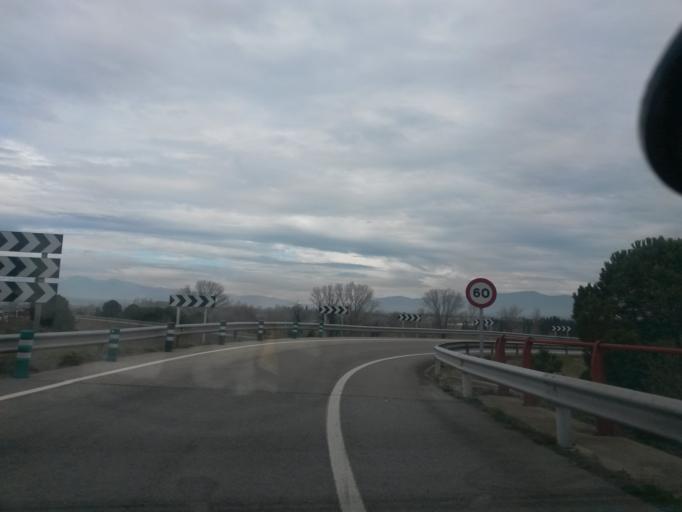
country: ES
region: Catalonia
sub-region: Provincia de Girona
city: Vilabertran
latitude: 42.2748
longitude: 2.9836
